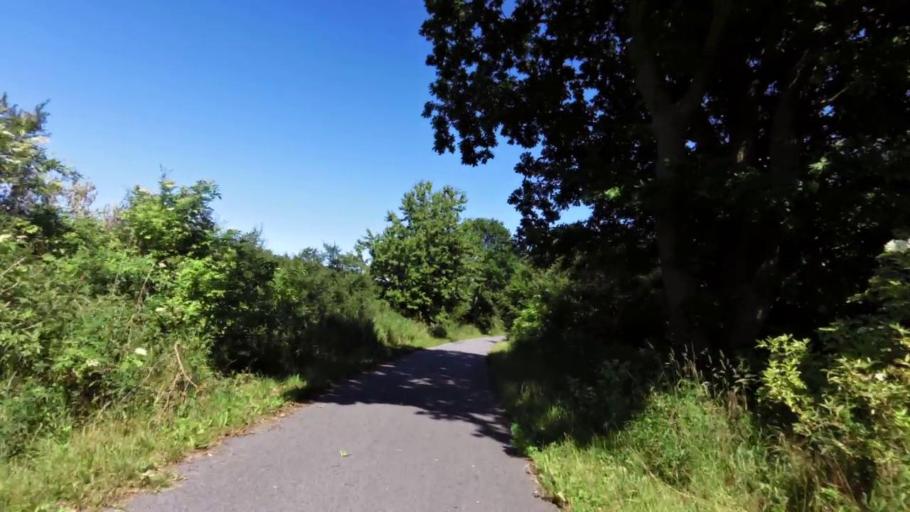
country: PL
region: West Pomeranian Voivodeship
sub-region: Powiat bialogardzki
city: Karlino
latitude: 54.0558
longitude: 15.8123
